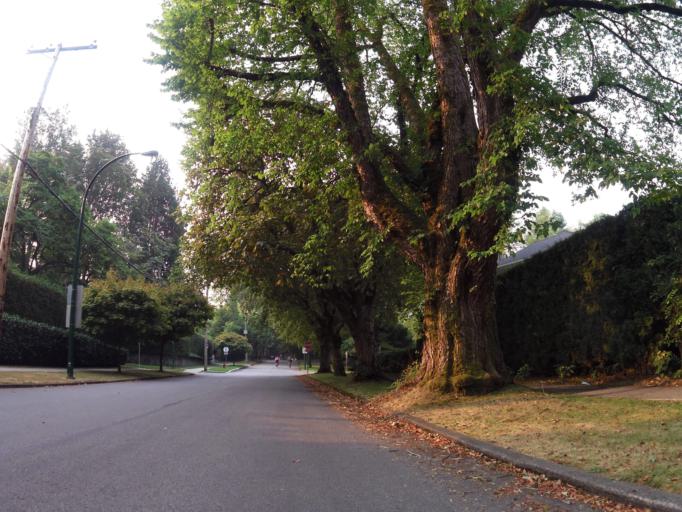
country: CA
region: British Columbia
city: Vancouver
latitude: 49.2534
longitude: -123.1485
